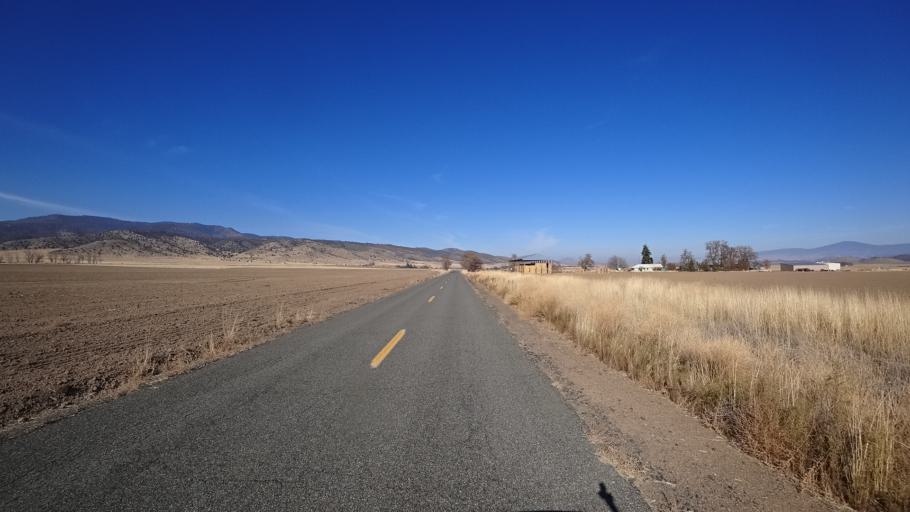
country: US
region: California
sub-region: Siskiyou County
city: Montague
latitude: 41.5572
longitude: -122.5463
